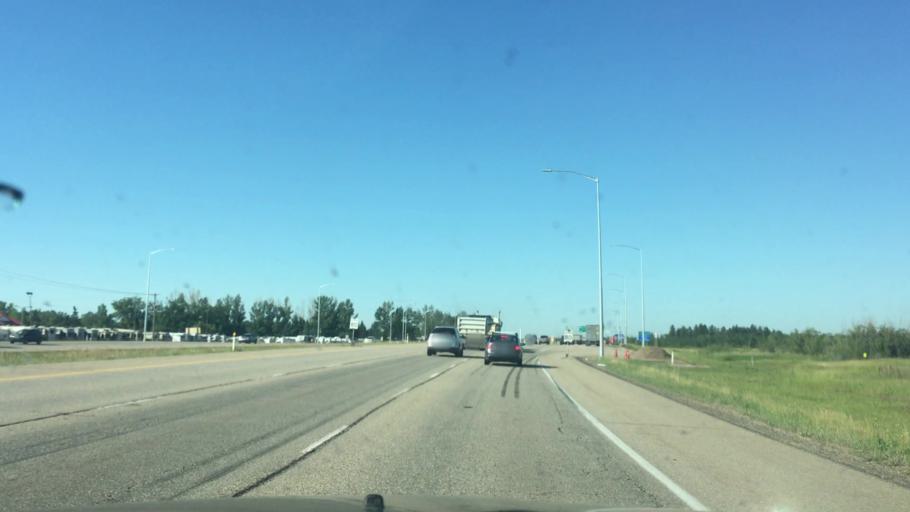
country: CA
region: Alberta
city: Leduc
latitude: 53.2772
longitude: -113.5534
